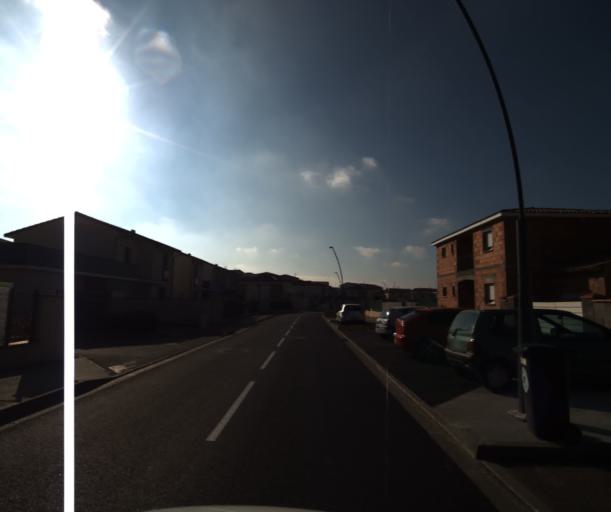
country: FR
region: Midi-Pyrenees
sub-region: Departement de la Haute-Garonne
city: Colomiers
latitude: 43.5999
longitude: 1.3520
